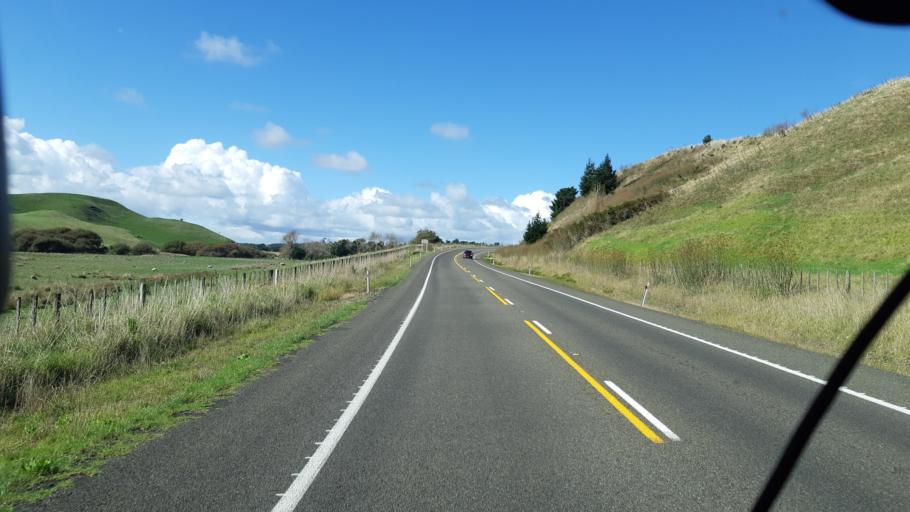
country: NZ
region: Manawatu-Wanganui
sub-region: Wanganui District
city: Wanganui
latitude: -39.9688
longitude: 175.1051
